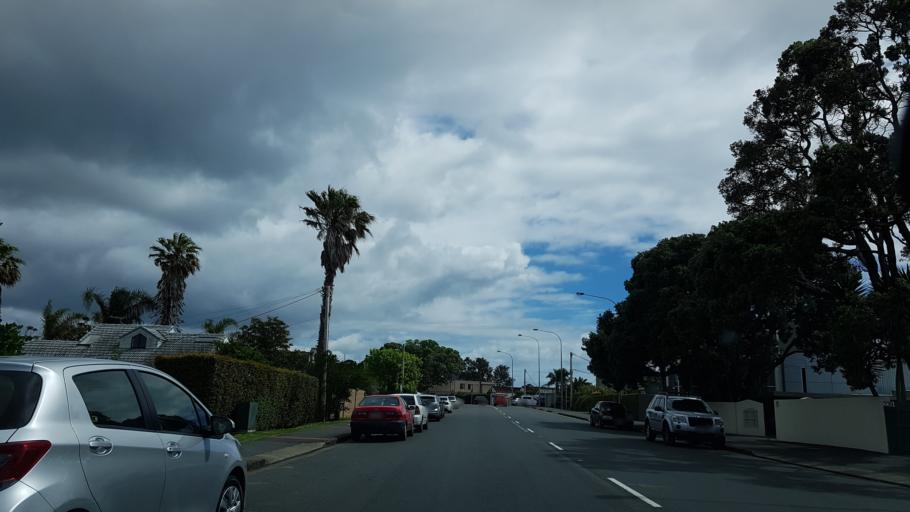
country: NZ
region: Auckland
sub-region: Auckland
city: North Shore
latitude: -36.7778
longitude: 174.7750
